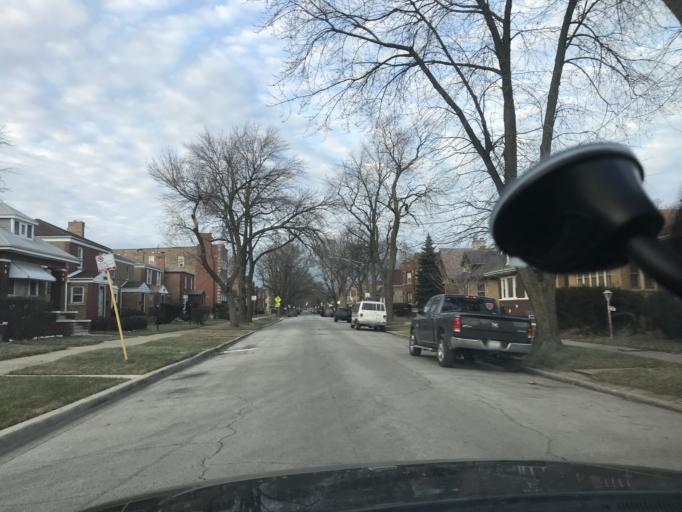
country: US
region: Indiana
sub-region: Lake County
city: Whiting
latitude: 41.7448
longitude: -87.5746
